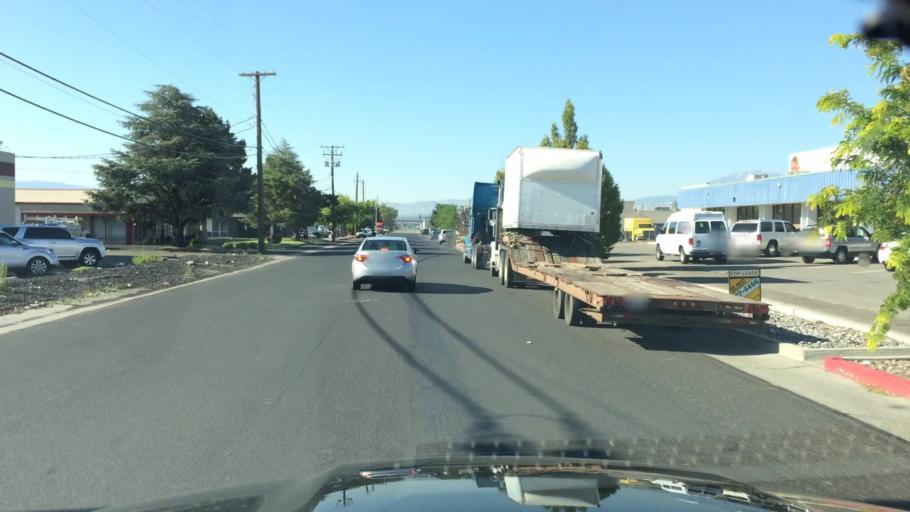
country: US
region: Nevada
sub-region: Washoe County
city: Sparks
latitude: 39.5166
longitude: -119.7754
